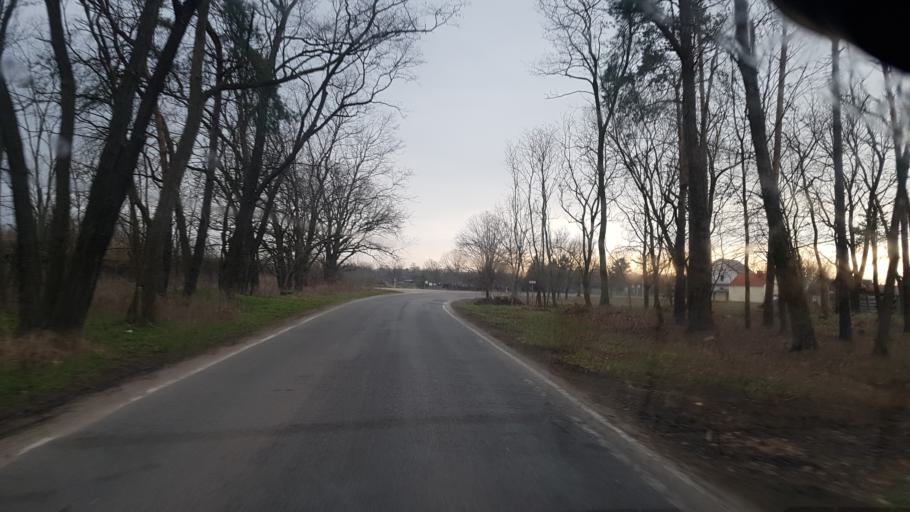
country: DE
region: Brandenburg
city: Cottbus
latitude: 51.7635
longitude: 14.4089
